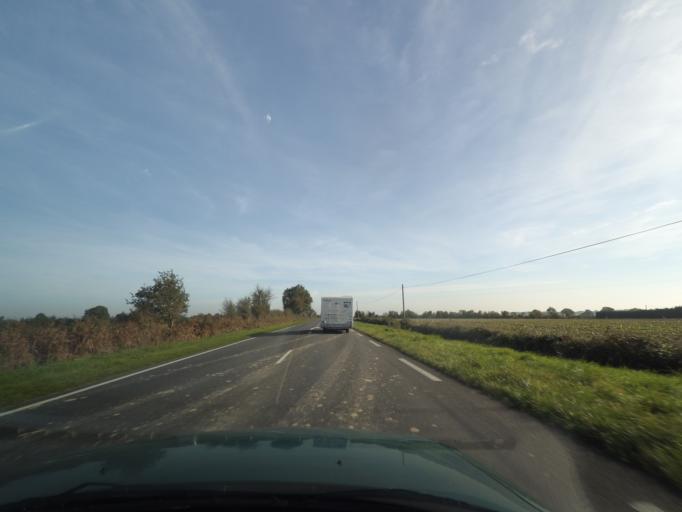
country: FR
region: Pays de la Loire
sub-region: Departement de Maine-et-Loire
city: Le Longeron
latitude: 47.0404
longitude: -1.0782
